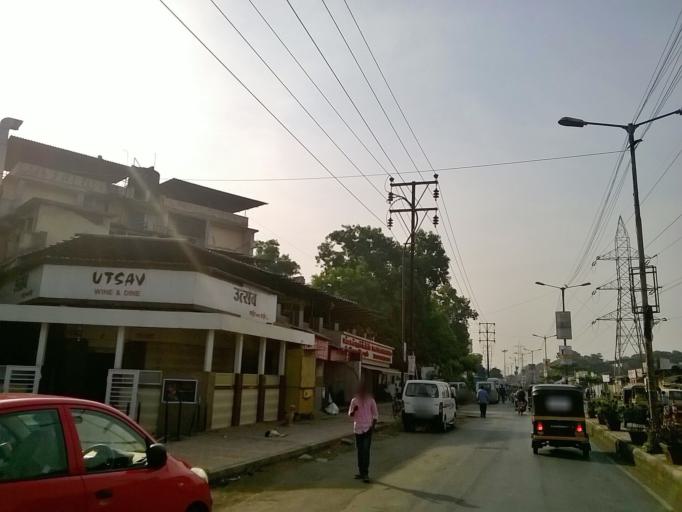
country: IN
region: Maharashtra
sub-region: Raigarh
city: Panvel
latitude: 18.9928
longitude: 73.1216
